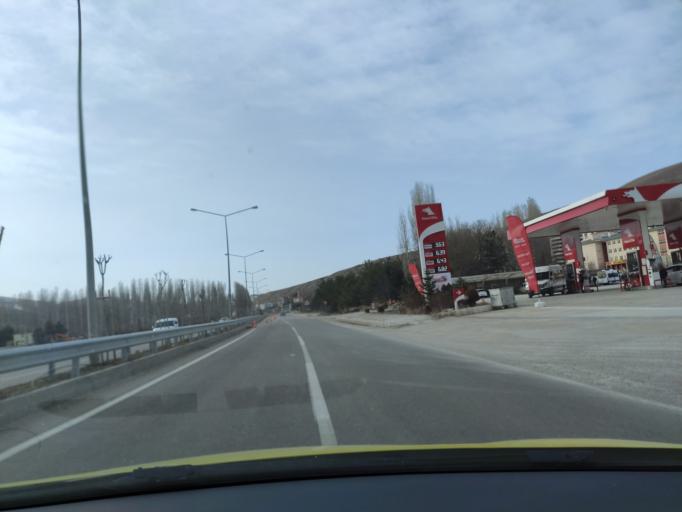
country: TR
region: Bayburt
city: Bayburt
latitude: 40.2391
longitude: 40.2501
